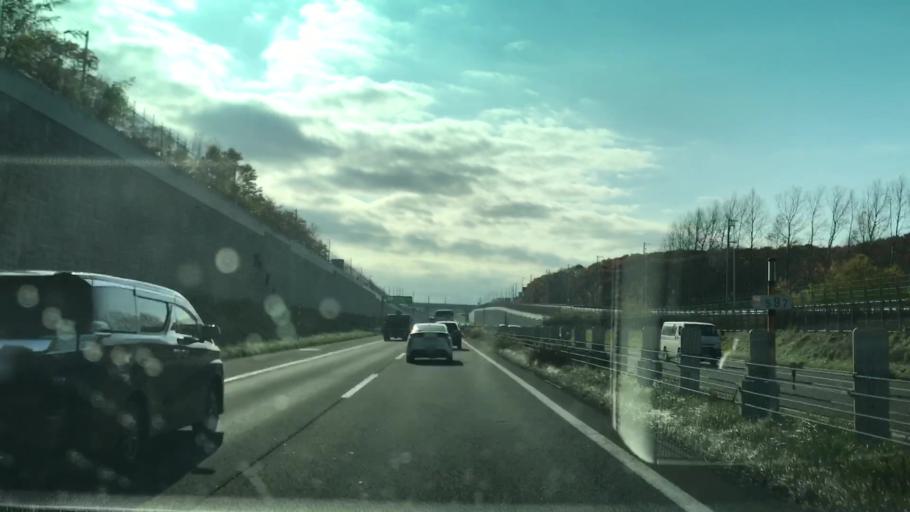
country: JP
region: Hokkaido
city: Kitahiroshima
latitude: 42.9992
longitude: 141.4682
